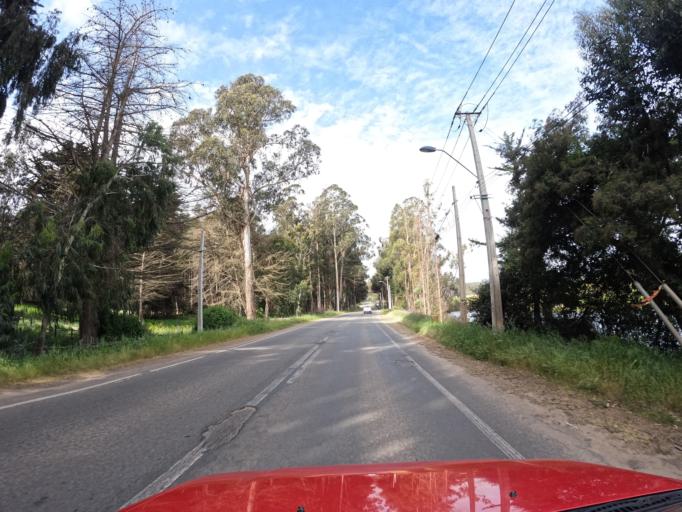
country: CL
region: O'Higgins
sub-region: Provincia de Colchagua
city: Santa Cruz
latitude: -34.3843
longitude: -71.9828
